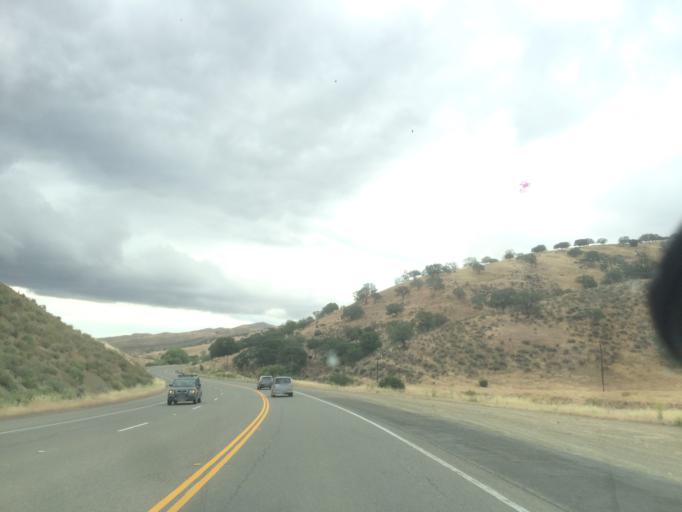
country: US
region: California
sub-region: San Luis Obispo County
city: Shandon
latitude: 35.7740
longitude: -120.1799
